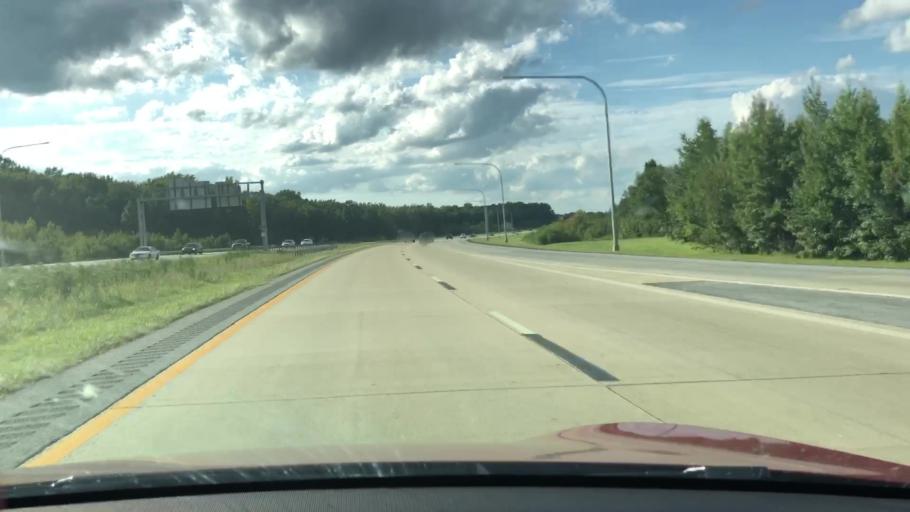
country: US
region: Delaware
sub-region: Kent County
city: Clayton
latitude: 39.3355
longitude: -75.6330
